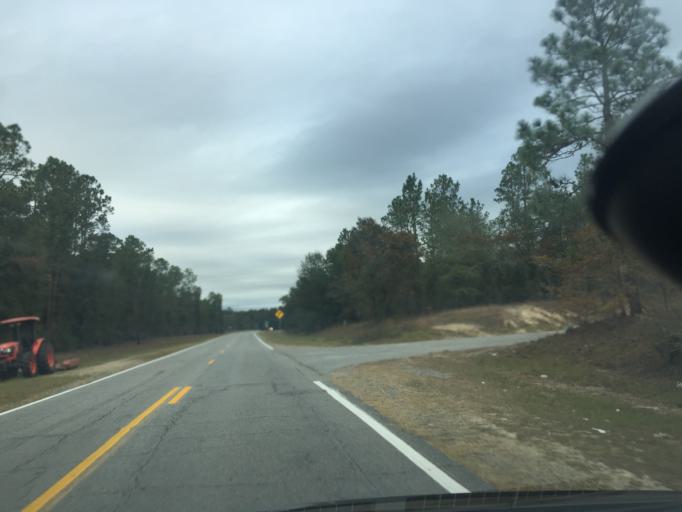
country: US
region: Georgia
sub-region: Chatham County
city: Bloomingdale
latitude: 32.1010
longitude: -81.3818
